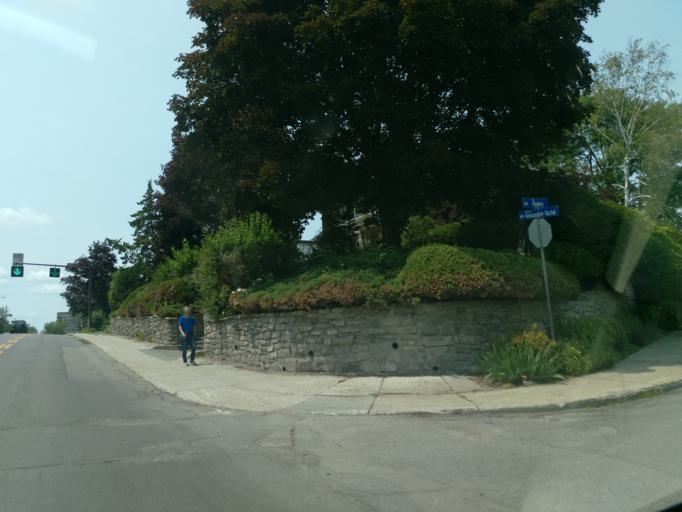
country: CA
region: Ontario
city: Ottawa
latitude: 45.4241
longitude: -75.7270
